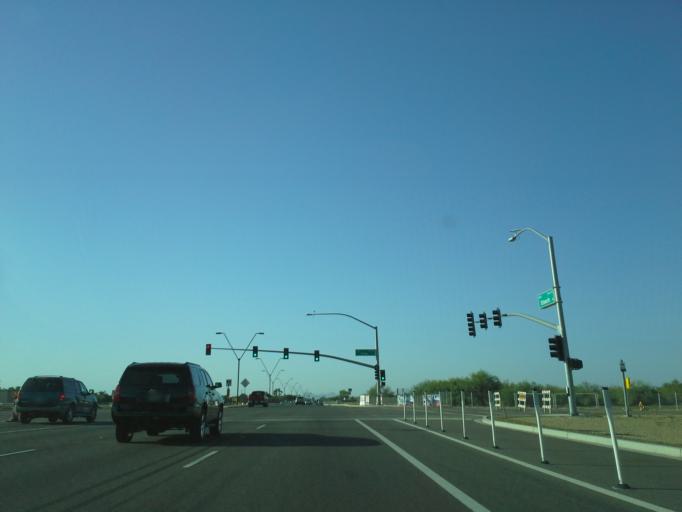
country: US
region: Arizona
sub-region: Maricopa County
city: Queen Creek
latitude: 33.2190
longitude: -111.6343
